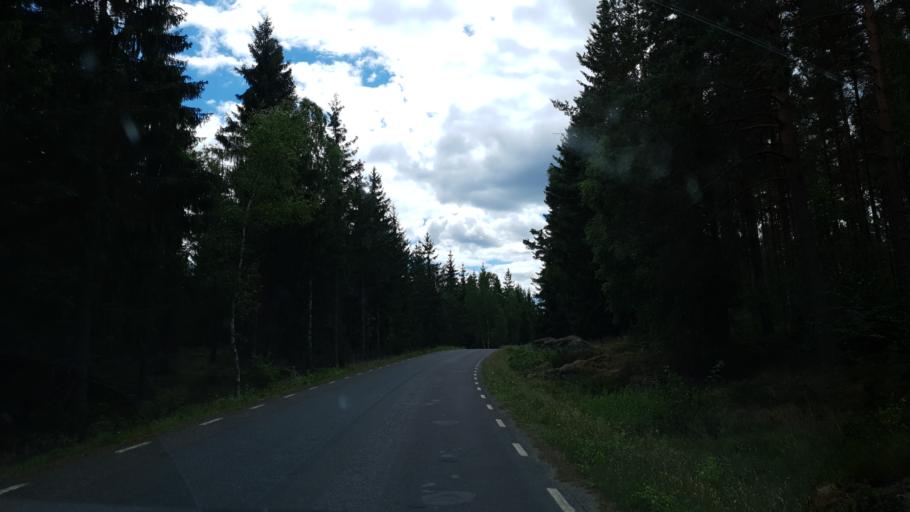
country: SE
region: Kalmar
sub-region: Hultsfreds Kommun
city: Virserum
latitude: 57.0828
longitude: 15.6106
